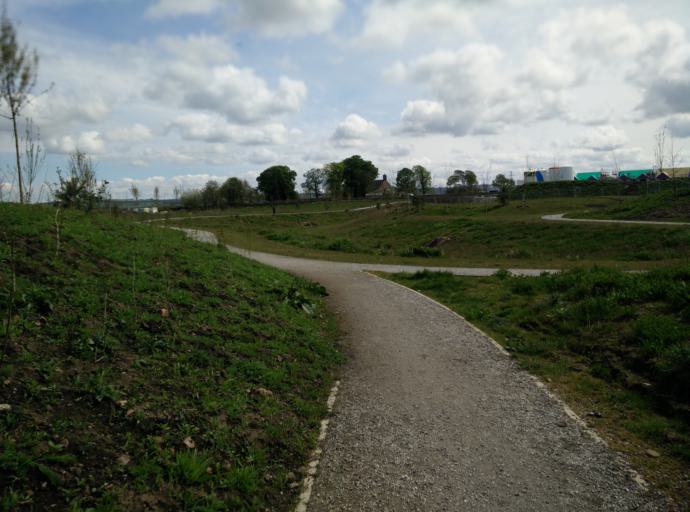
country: GB
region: Scotland
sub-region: Midlothian
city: Dalkeith
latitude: 55.9135
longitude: -3.1008
